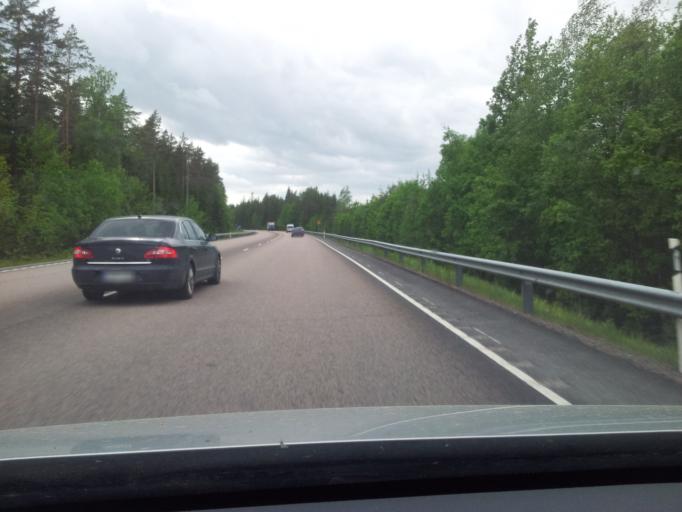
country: FI
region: South Karelia
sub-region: Lappeenranta
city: Taavetti
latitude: 60.9173
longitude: 27.4215
